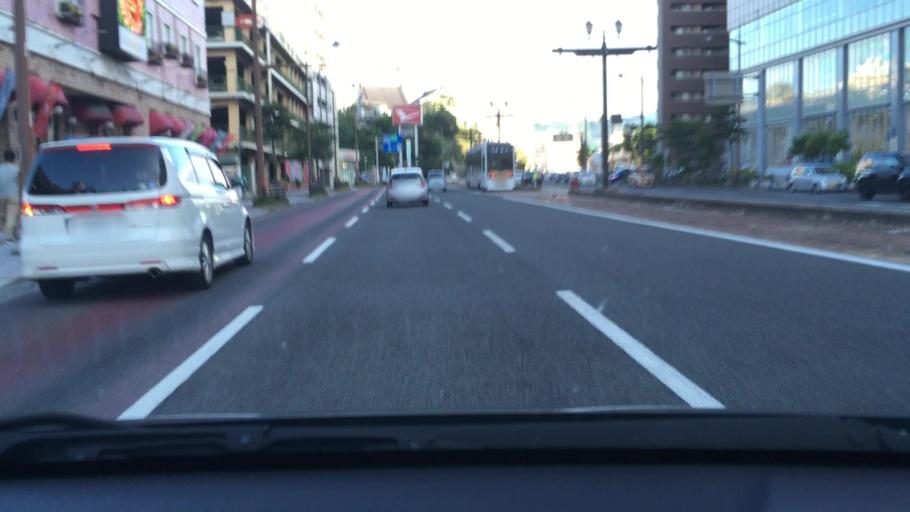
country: JP
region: Nagasaki
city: Nagasaki-shi
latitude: 32.7627
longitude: 129.8653
